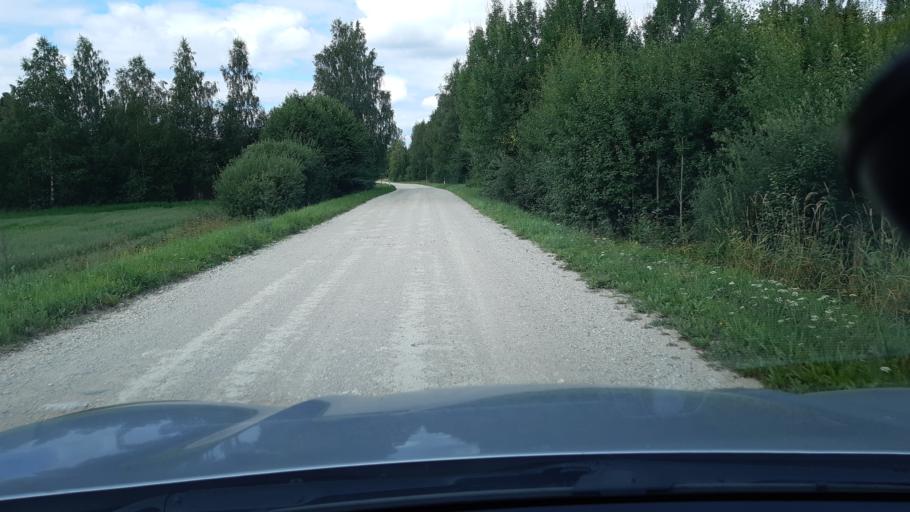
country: EE
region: Paernumaa
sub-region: Vaendra vald (alev)
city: Vandra
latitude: 58.7885
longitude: 25.0219
